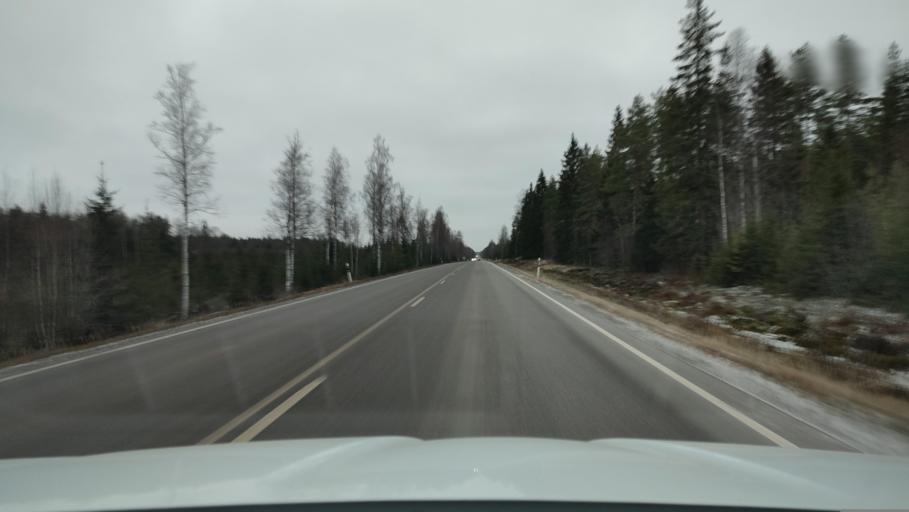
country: FI
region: Ostrobothnia
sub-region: Sydosterbotten
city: Naerpes
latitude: 62.5061
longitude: 21.4511
